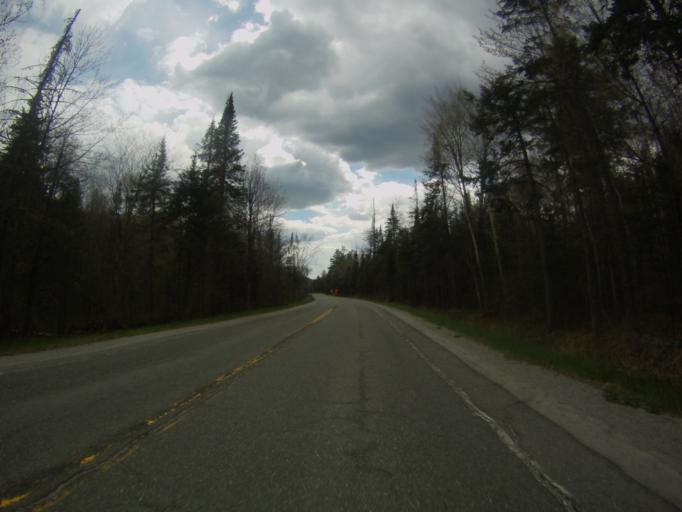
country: US
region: New York
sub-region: Essex County
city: Mineville
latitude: 44.0943
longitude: -73.5761
